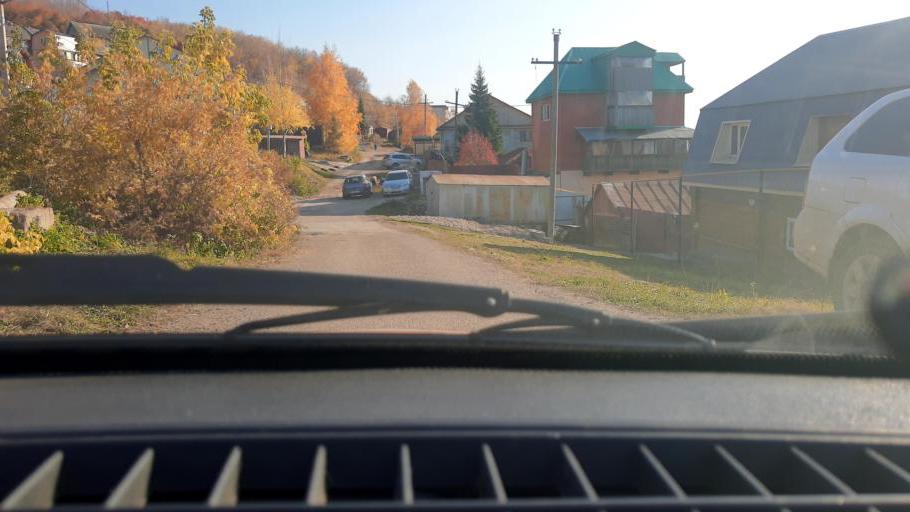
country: RU
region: Bashkortostan
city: Ufa
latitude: 54.6999
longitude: 55.9741
